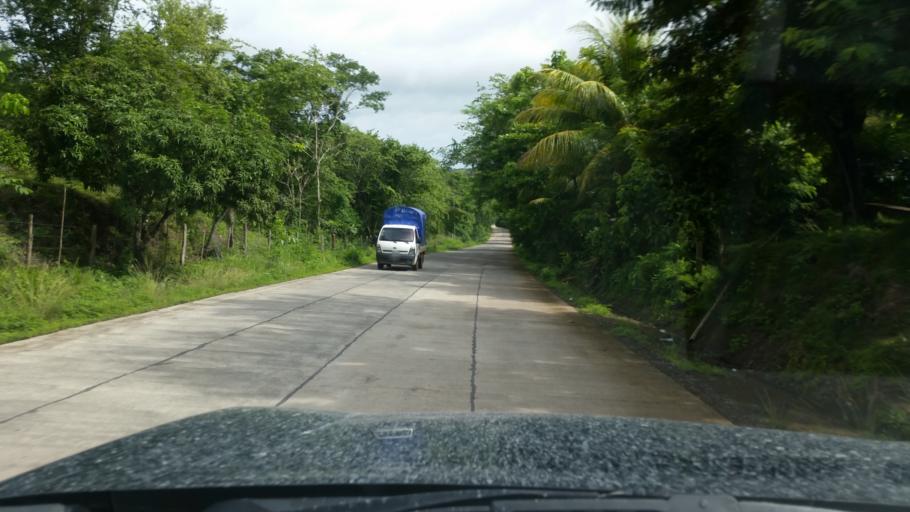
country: NI
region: Atlantico Norte (RAAN)
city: Siuna
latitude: 13.5626
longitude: -84.8171
